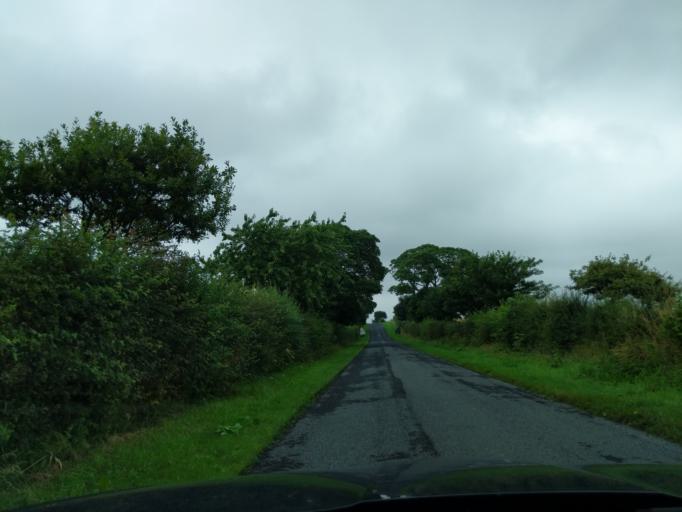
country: GB
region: England
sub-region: Northumberland
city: Ford
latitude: 55.6984
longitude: -2.1424
